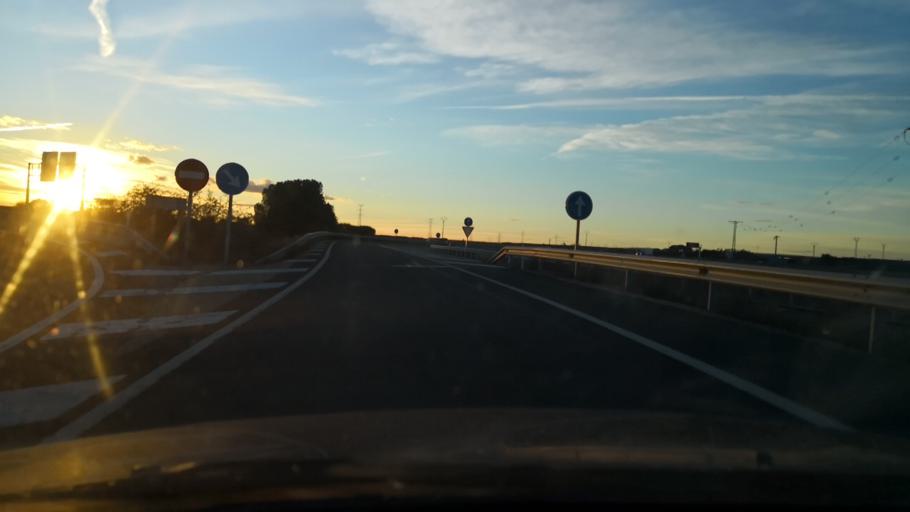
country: ES
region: Castille and Leon
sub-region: Provincia de Valladolid
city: Tordesillas
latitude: 41.5145
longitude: -5.0220
